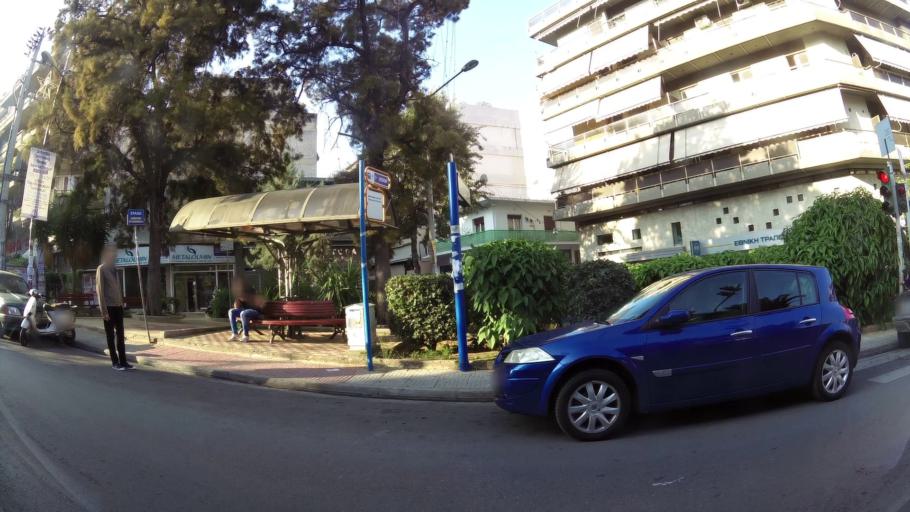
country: GR
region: Attica
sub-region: Nomarchia Athinas
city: Kaisariani
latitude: 37.9745
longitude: 23.7662
